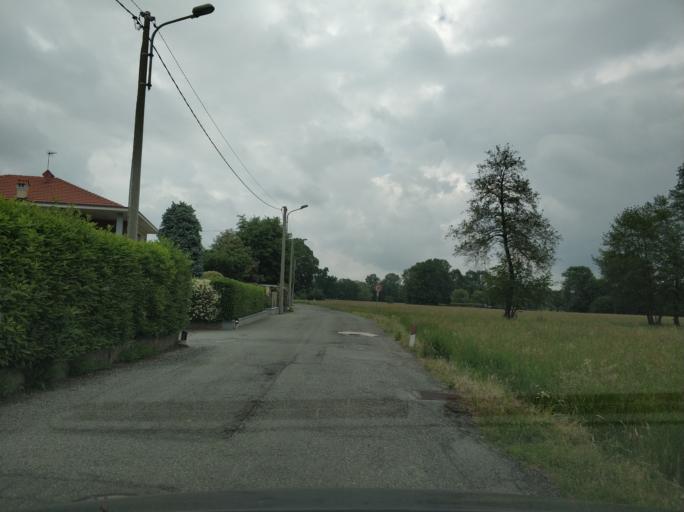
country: IT
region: Piedmont
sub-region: Provincia di Torino
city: Nole
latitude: 45.2431
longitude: 7.5822
